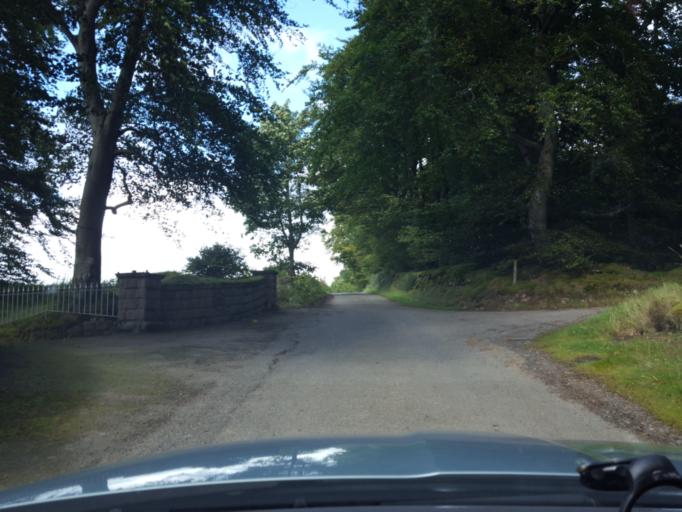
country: GB
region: Scotland
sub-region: Aberdeenshire
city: Banchory
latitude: 57.1485
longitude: -2.4997
